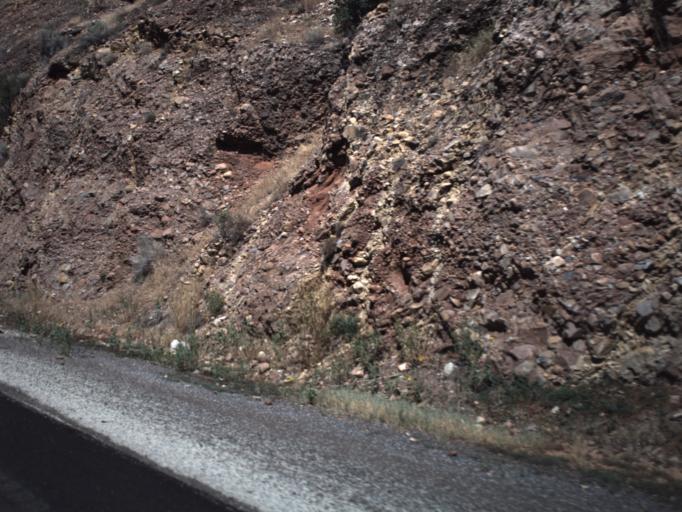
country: US
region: Utah
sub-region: Utah County
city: Mapleton
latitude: 39.9917
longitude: -111.3923
